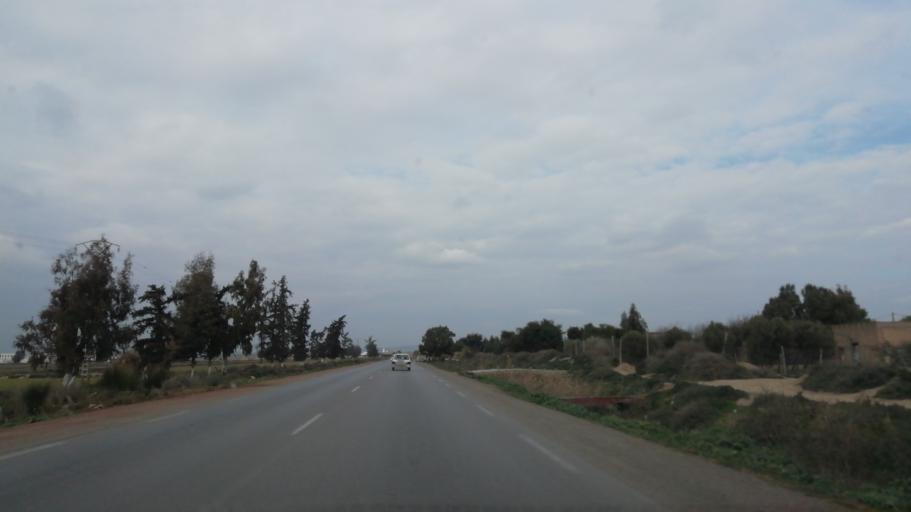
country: DZ
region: Mostaganem
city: Mostaganem
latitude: 35.6870
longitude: 0.0564
